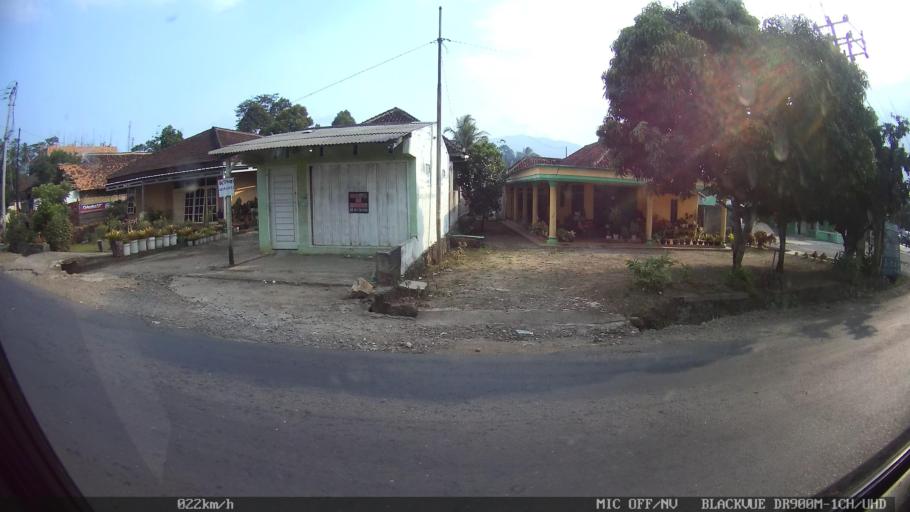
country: ID
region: Lampung
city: Natar
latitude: -5.3638
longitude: 105.1859
